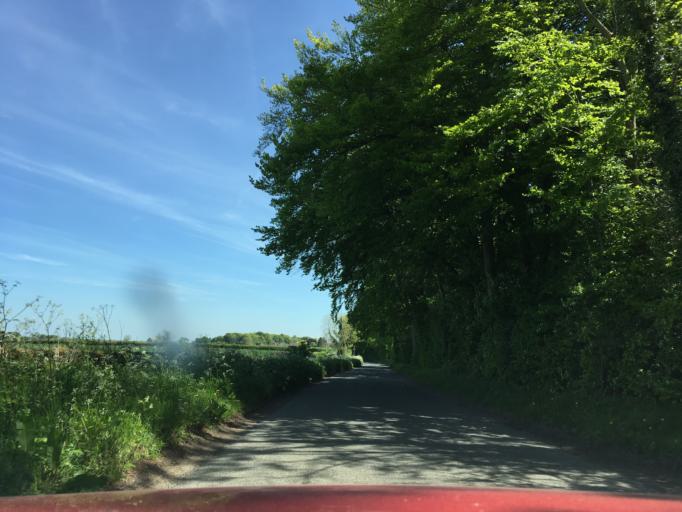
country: GB
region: England
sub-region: Gloucestershire
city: Coates
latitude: 51.7119
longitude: -2.0400
